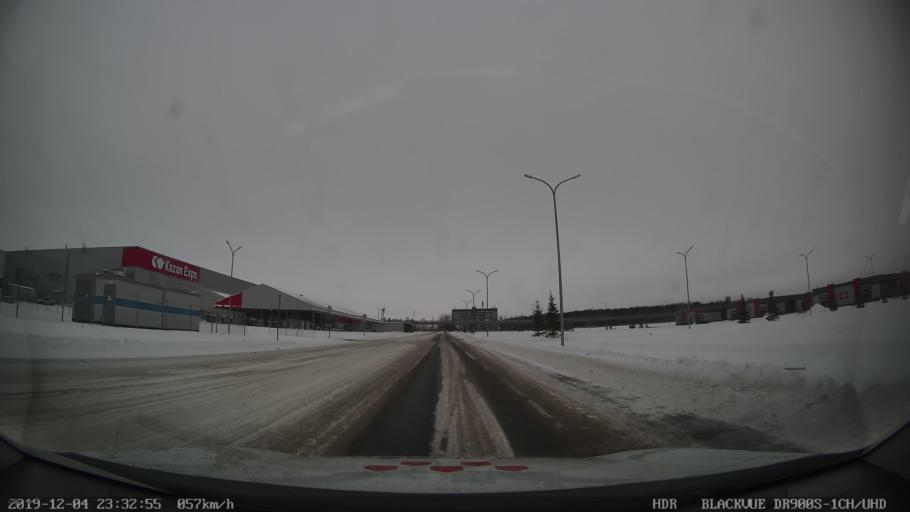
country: RU
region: Tatarstan
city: Stolbishchi
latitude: 55.6143
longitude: 49.2970
